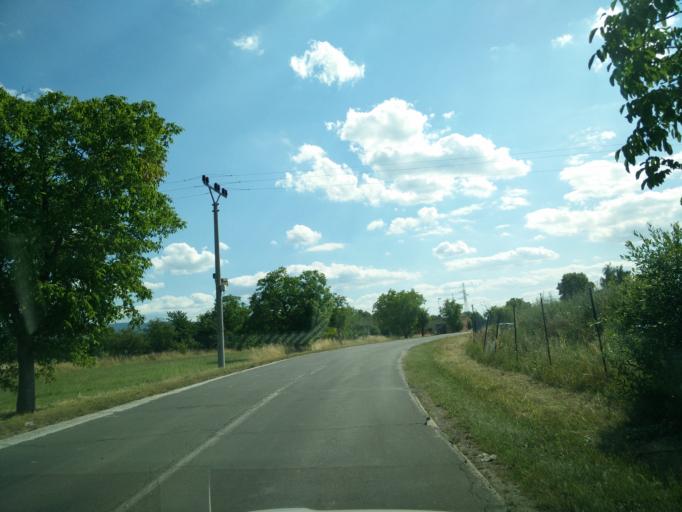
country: SK
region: Nitriansky
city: Prievidza
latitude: 48.7464
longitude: 18.6248
